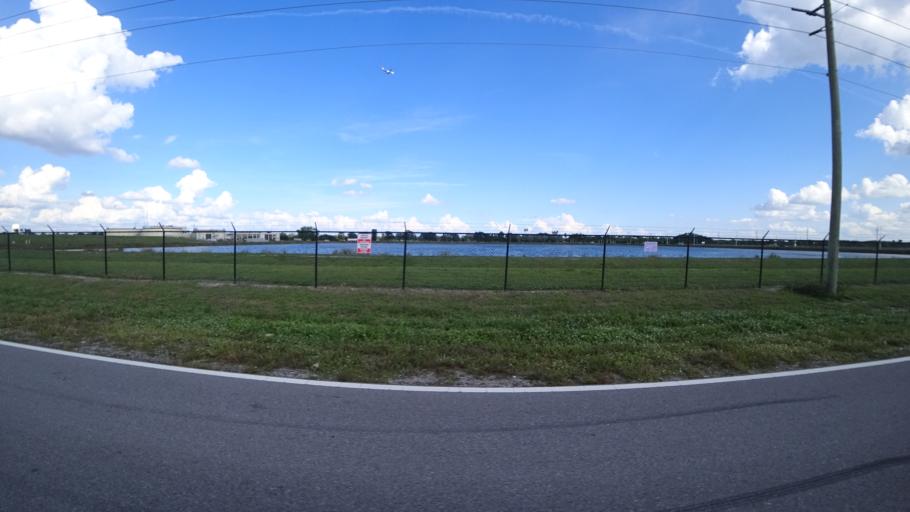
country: US
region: Florida
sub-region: Manatee County
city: Bayshore Gardens
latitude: 27.4497
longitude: -82.6285
